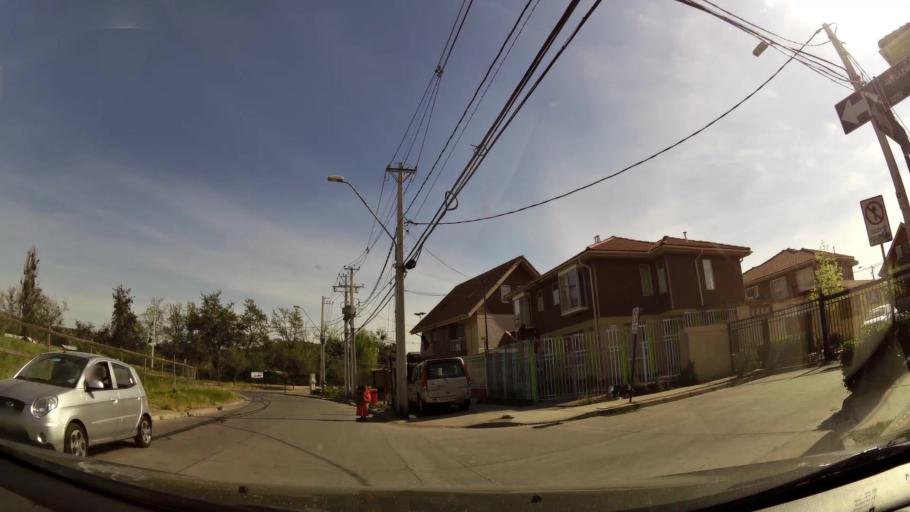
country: CL
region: Santiago Metropolitan
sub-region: Provincia de Cordillera
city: Puente Alto
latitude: -33.5934
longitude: -70.5499
